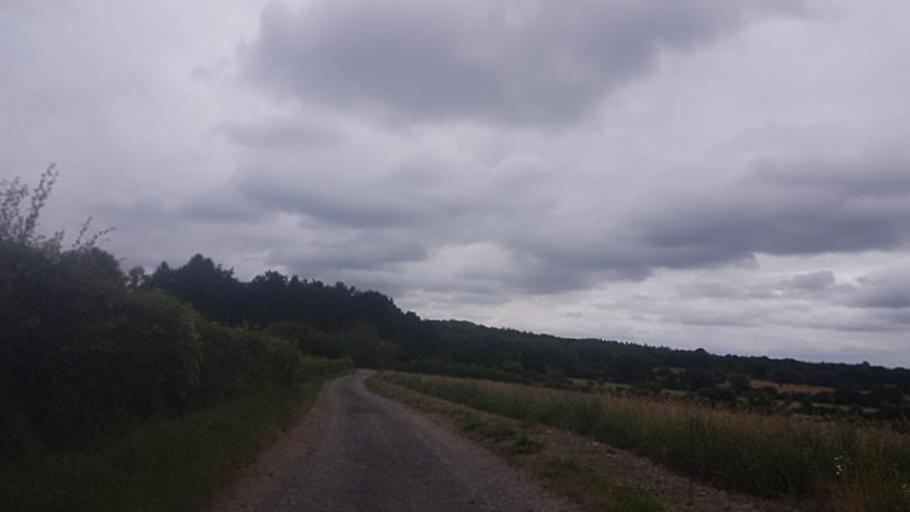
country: BE
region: Wallonia
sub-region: Province de Namur
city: Philippeville
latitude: 50.1054
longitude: 4.5795
